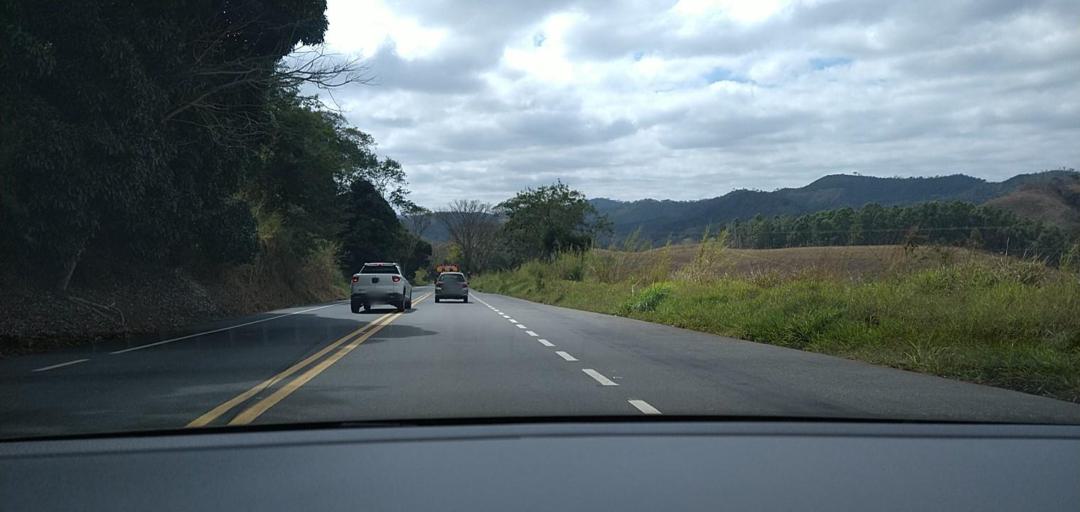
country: BR
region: Minas Gerais
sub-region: Ponte Nova
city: Ponte Nova
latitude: -20.5094
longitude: -42.8827
